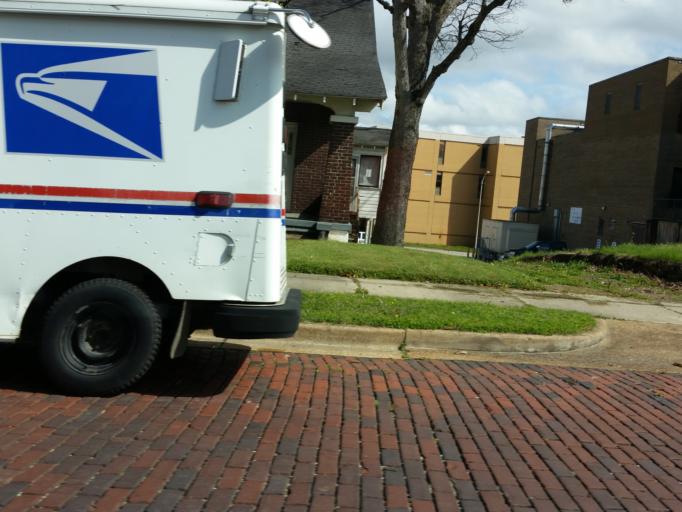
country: US
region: Missouri
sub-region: Butler County
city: Poplar Bluff
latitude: 36.7570
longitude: -90.3978
